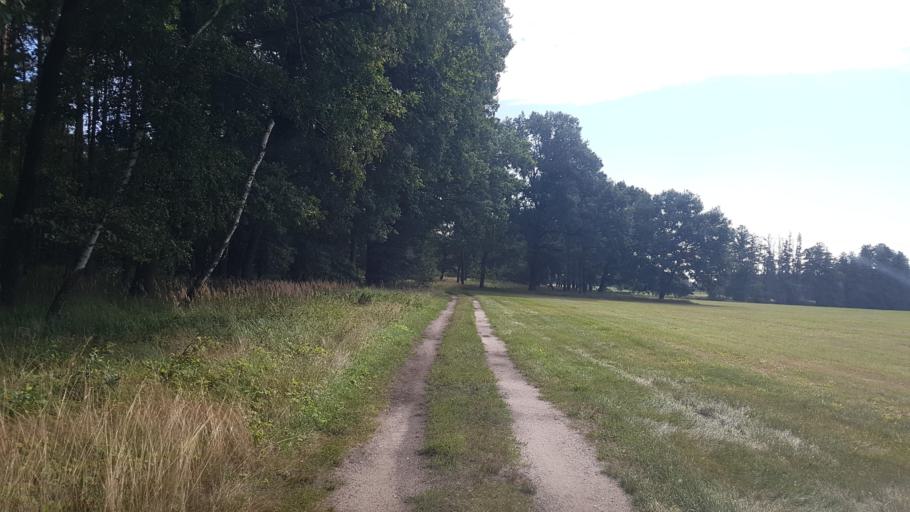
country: DE
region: Brandenburg
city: Bronkow
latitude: 51.6333
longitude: 13.8856
